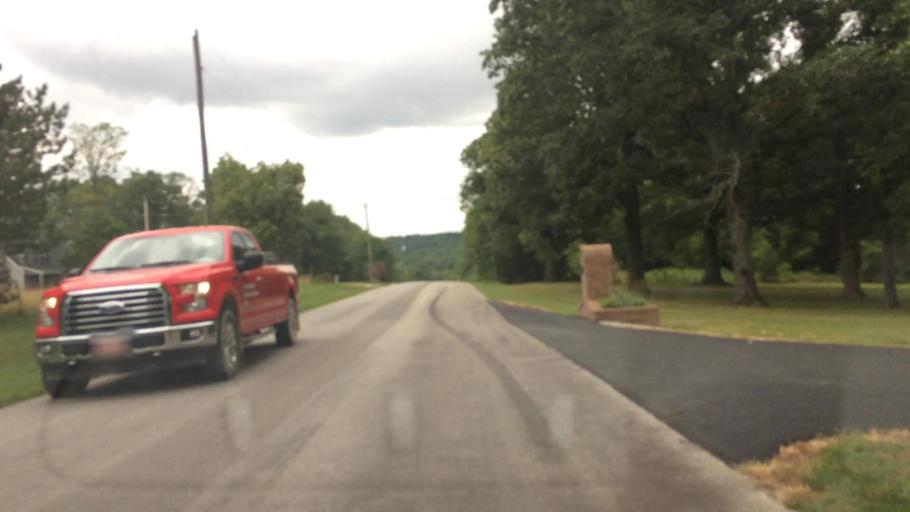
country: US
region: Missouri
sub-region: Webster County
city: Marshfield
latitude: 37.3090
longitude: -92.9846
